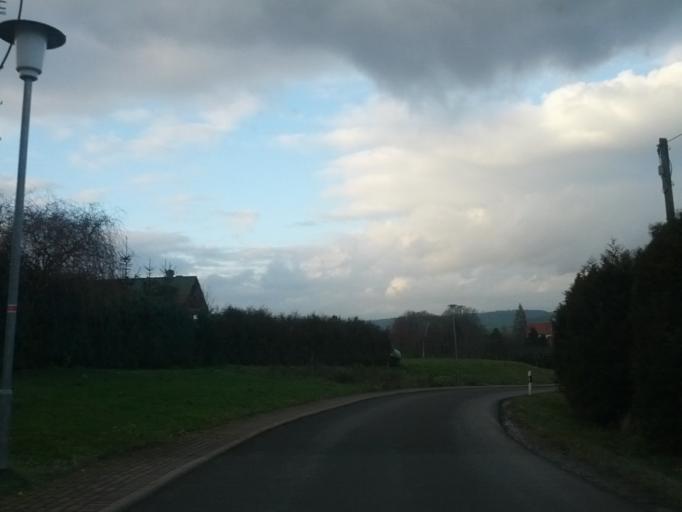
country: DE
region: Thuringia
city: Bischofroda
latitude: 51.0527
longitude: 10.3618
